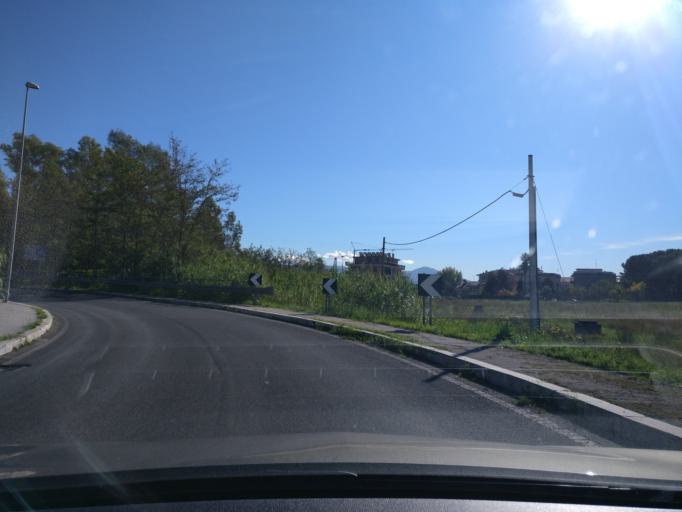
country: IT
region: Latium
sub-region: Citta metropolitana di Roma Capitale
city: Frascati
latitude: 41.8511
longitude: 12.6203
